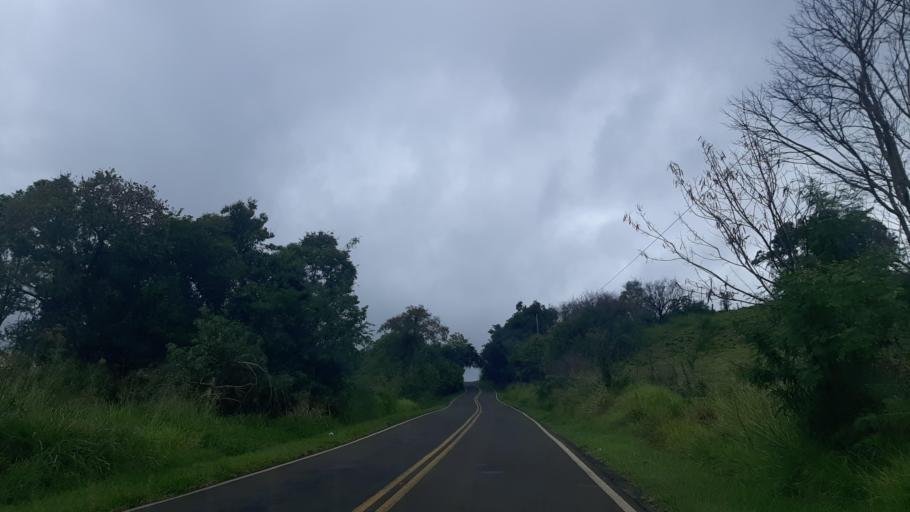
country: BR
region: Parana
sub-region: Ampere
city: Ampere
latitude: -25.9853
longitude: -53.4422
